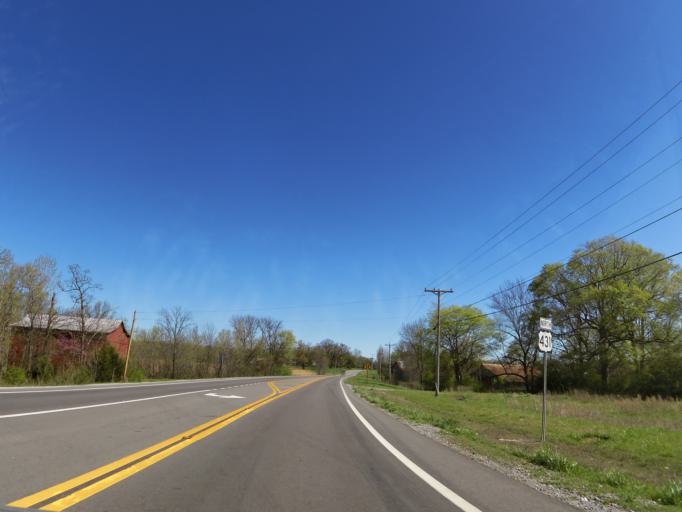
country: US
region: Tennessee
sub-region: Robertson County
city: Springfield
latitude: 36.5355
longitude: -86.8811
